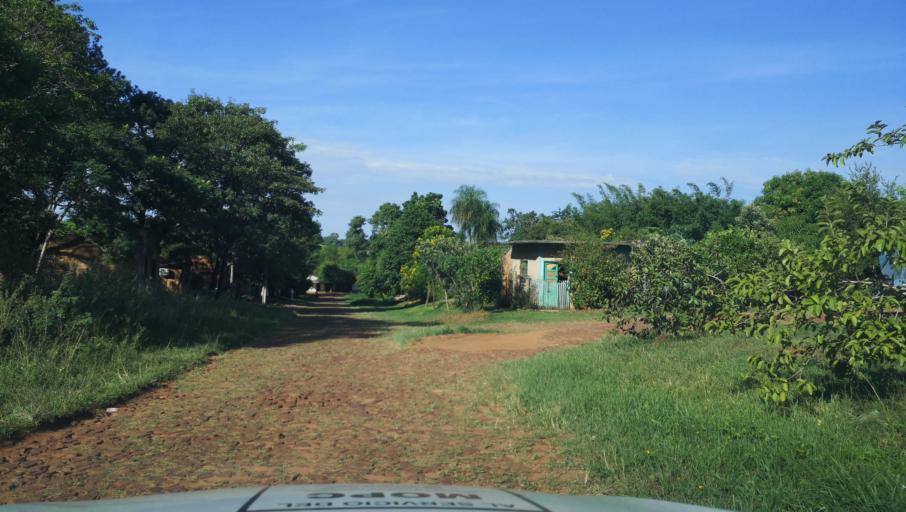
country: PY
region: Misiones
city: Santa Maria
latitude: -26.8824
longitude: -57.0087
